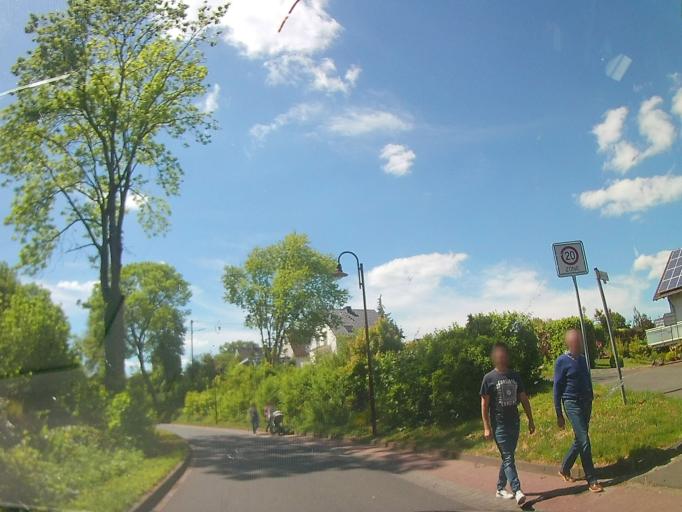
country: DE
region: Rheinland-Pfalz
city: Dierdorf
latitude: 50.5459
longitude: 7.6505
